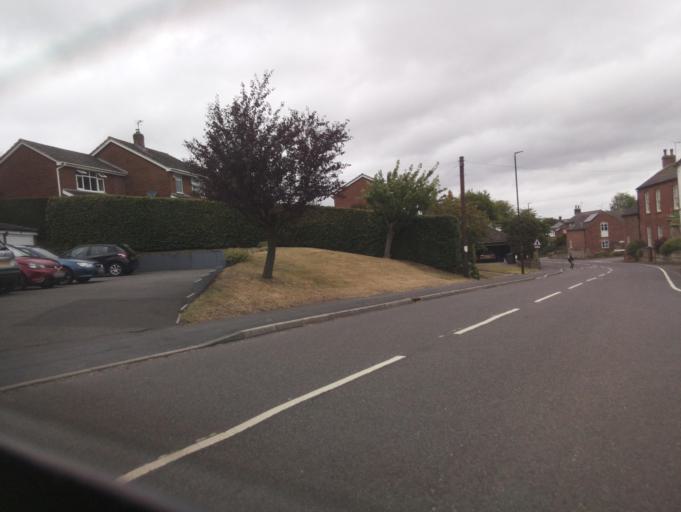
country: GB
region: England
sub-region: Derbyshire
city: Findern
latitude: 52.8721
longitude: -1.5440
